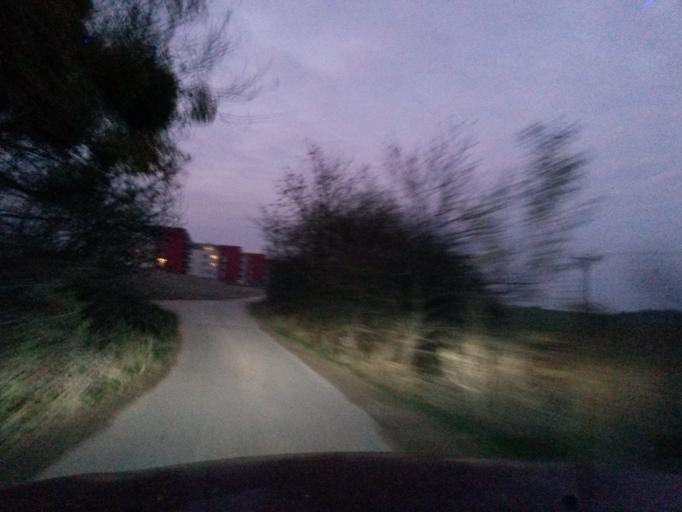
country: SK
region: Kosicky
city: Kosice
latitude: 48.7174
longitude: 21.2937
